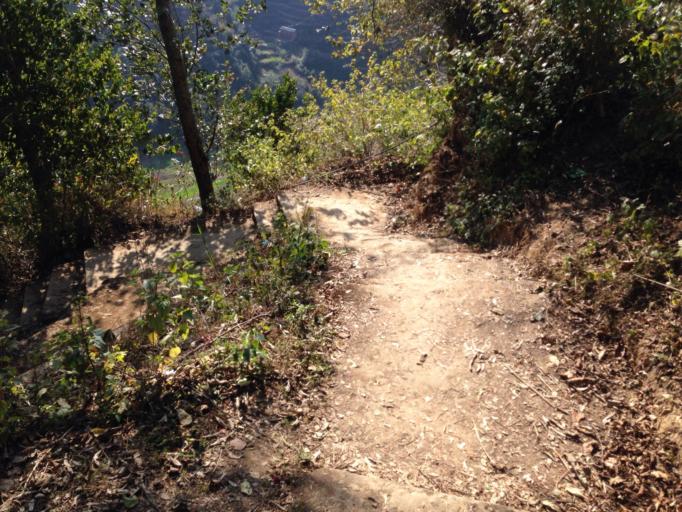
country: NP
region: Central Region
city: Kirtipur
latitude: 27.7320
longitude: 85.2644
